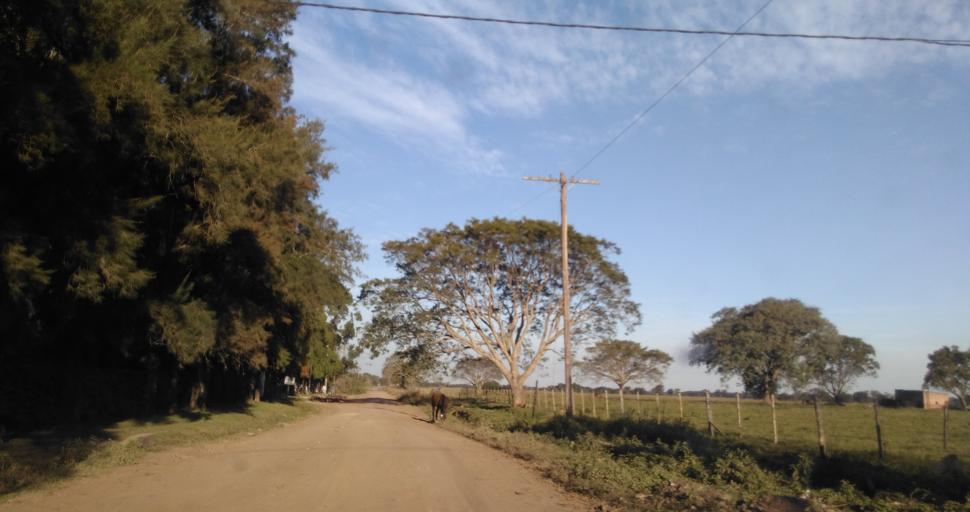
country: AR
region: Chaco
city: Colonia Benitez
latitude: -27.3359
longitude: -58.9430
